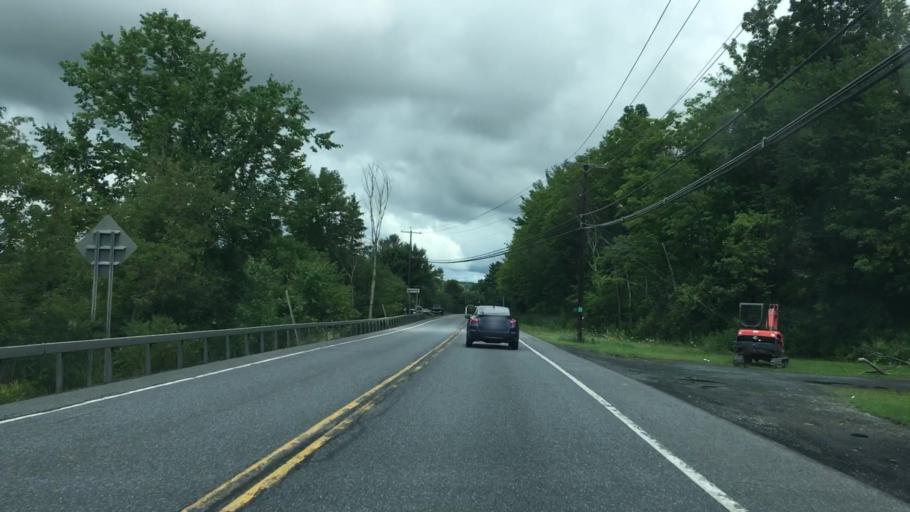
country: US
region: New York
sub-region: Rensselaer County
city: Hoosick Falls
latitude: 42.8362
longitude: -73.4839
